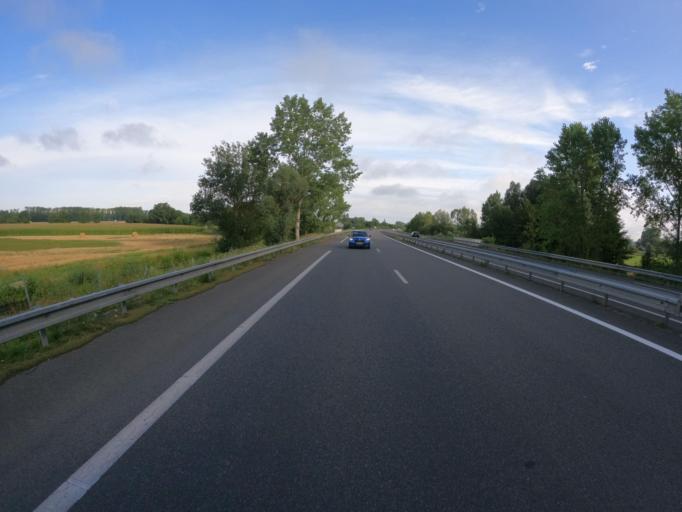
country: FR
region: Pays de la Loire
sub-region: Departement de Maine-et-Loire
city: Vivy
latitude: 47.3003
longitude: -0.0308
